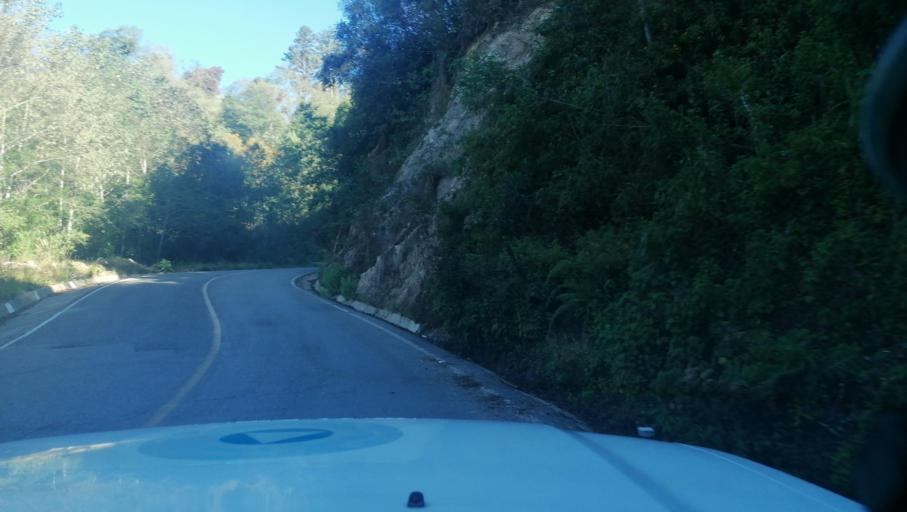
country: MX
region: Chiapas
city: Motozintla de Mendoza
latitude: 15.2360
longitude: -92.2343
